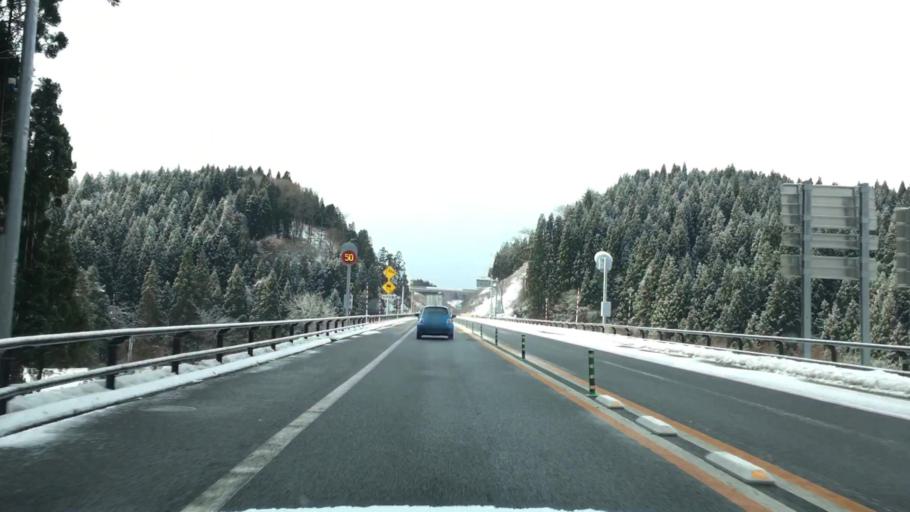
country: JP
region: Akita
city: Takanosu
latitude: 40.2188
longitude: 140.4264
